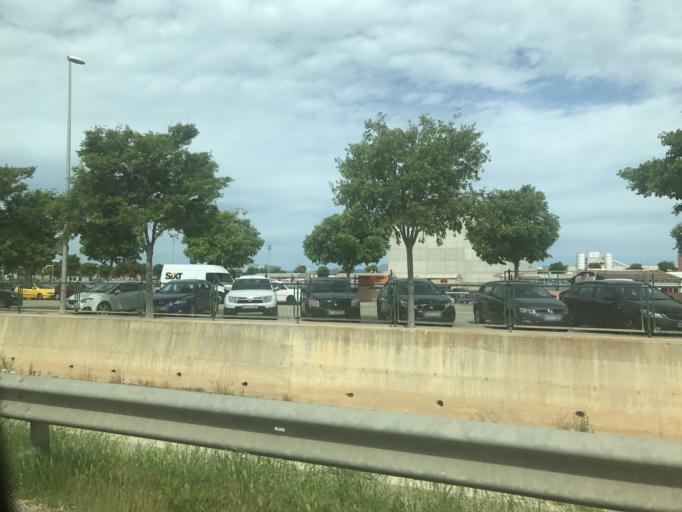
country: ES
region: Balearic Islands
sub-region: Illes Balears
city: s'Arenal
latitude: 39.5387
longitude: 2.7418
